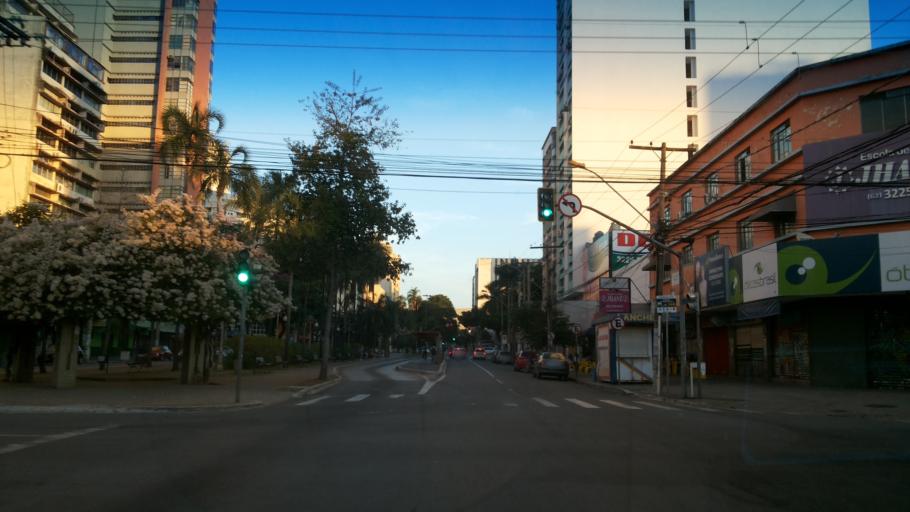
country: BR
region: Goias
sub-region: Goiania
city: Goiania
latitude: -16.6737
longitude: -49.2586
